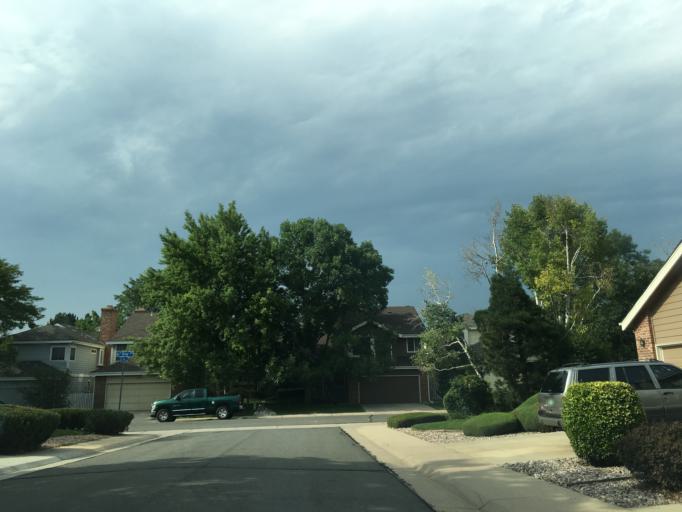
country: US
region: Colorado
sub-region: Jefferson County
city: Lakewood
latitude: 39.6738
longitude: -105.0615
